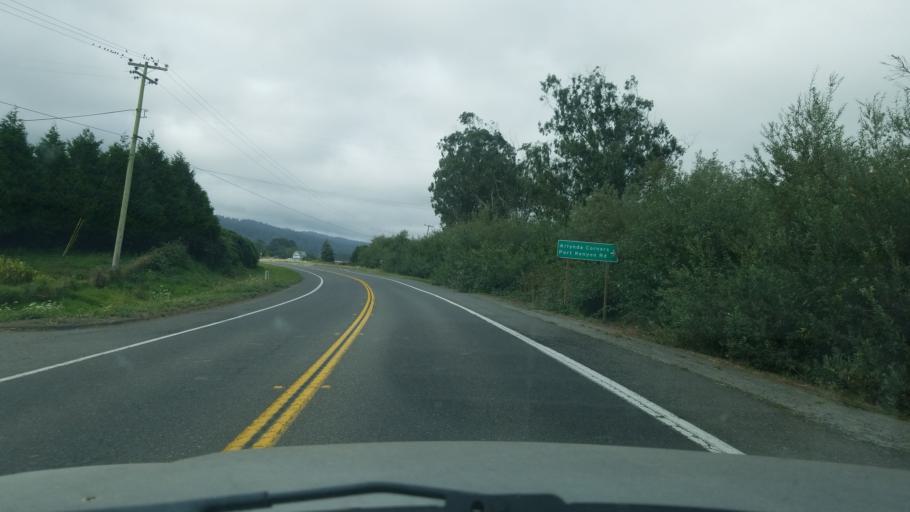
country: US
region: California
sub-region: Humboldt County
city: Ferndale
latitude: 40.5956
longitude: -124.2462
